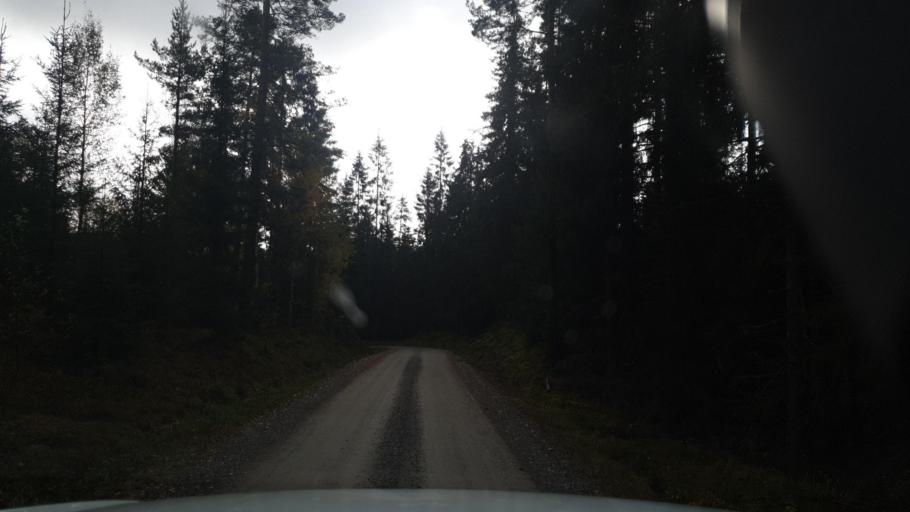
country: SE
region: Vaermland
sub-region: Arvika Kommun
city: Arvika
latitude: 59.5387
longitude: 12.4450
